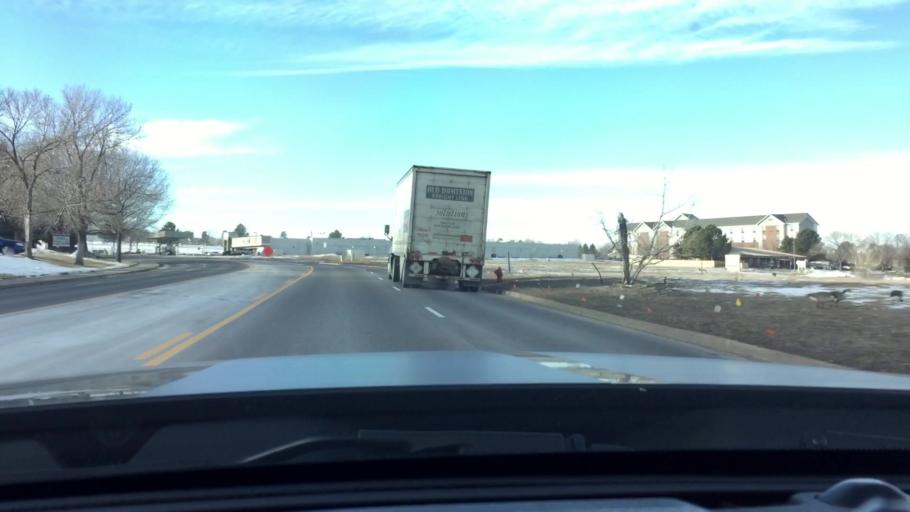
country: US
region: Colorado
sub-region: Adams County
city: Northglenn
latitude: 39.9170
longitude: -105.0055
